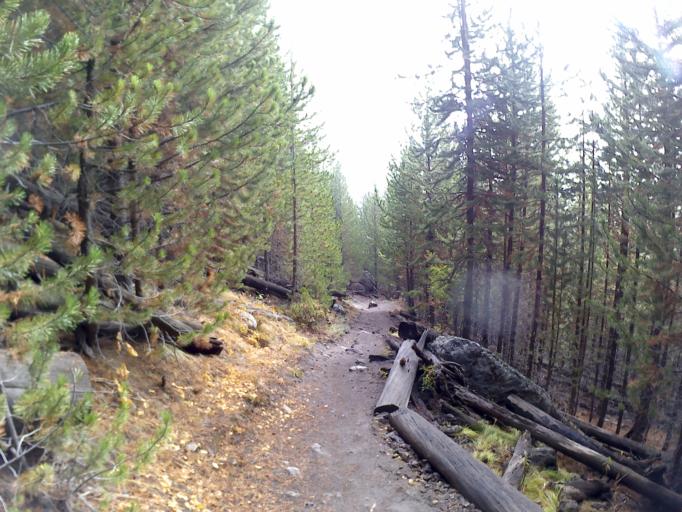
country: US
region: Montana
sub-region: Gallatin County
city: West Yellowstone
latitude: 44.4858
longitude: -110.8665
